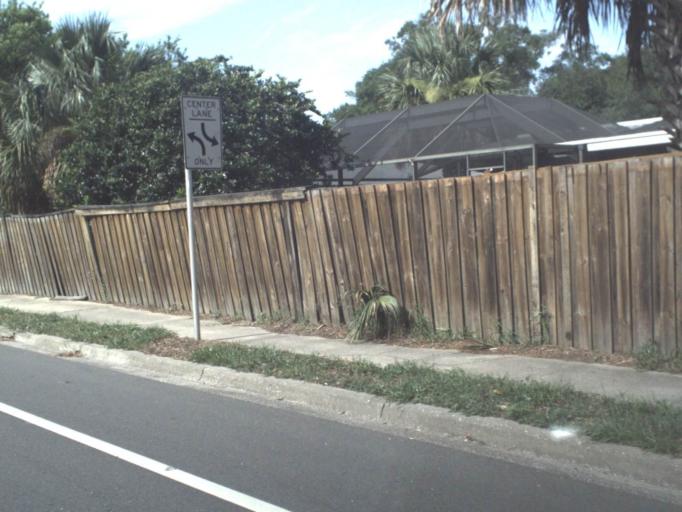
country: US
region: Florida
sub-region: Clay County
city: Orange Park
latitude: 30.2274
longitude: -81.6165
